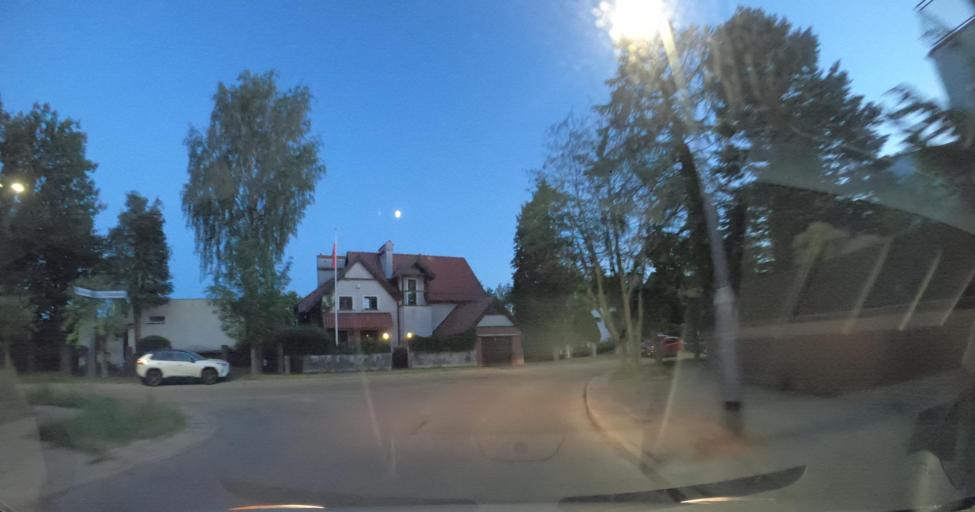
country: PL
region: Pomeranian Voivodeship
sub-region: Gdynia
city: Wielki Kack
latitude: 54.4270
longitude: 18.4657
